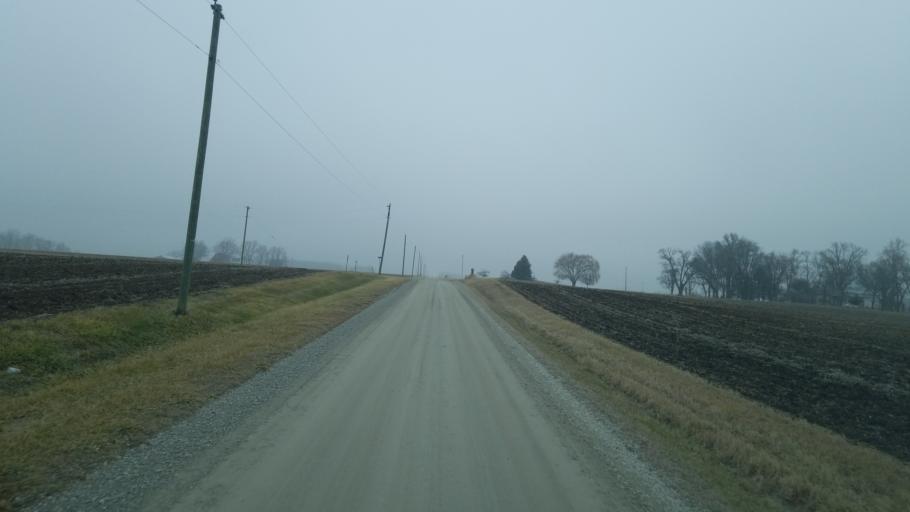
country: US
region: Indiana
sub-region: Adams County
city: Geneva
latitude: 40.6178
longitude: -85.0696
